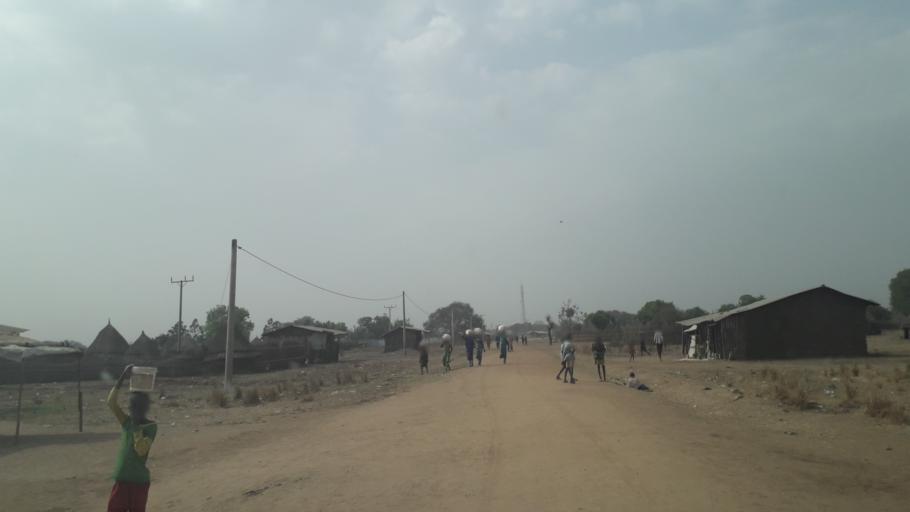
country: ET
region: Gambela
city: Gambela
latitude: 8.3071
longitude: 33.6871
